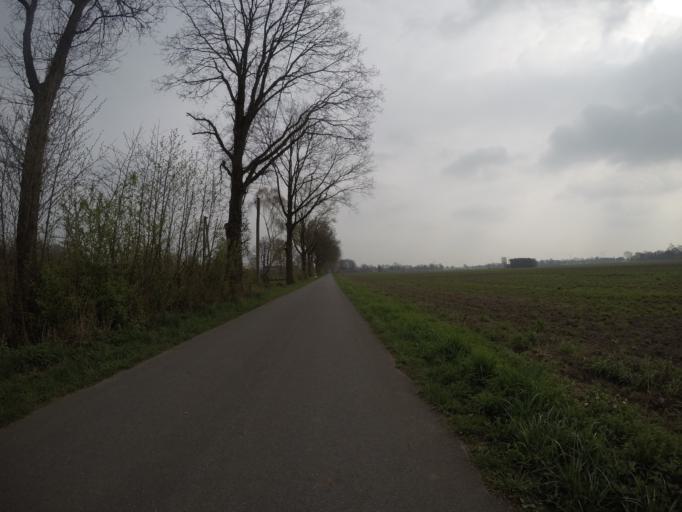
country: NL
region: Gelderland
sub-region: Gemeente Aalten
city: Aalten
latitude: 51.8739
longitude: 6.5295
